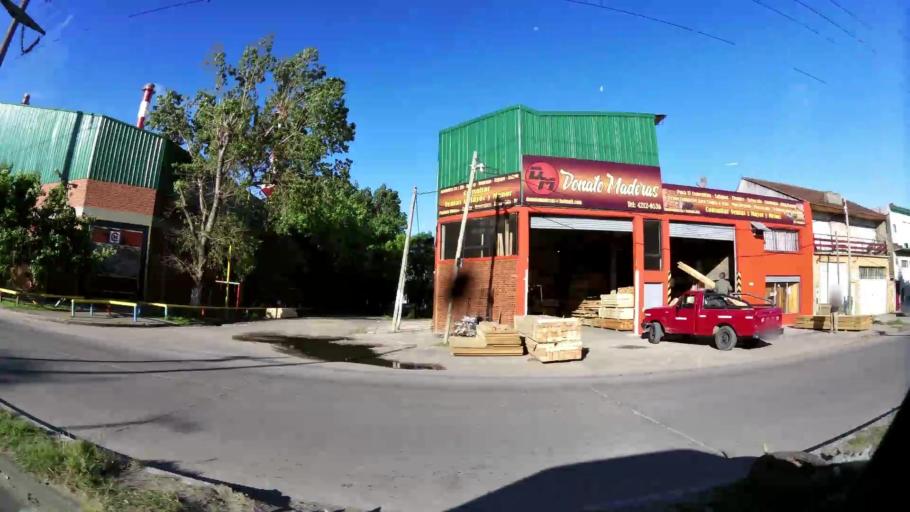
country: AR
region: Buenos Aires
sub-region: Partido de Almirante Brown
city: Adrogue
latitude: -34.7525
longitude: -58.3381
